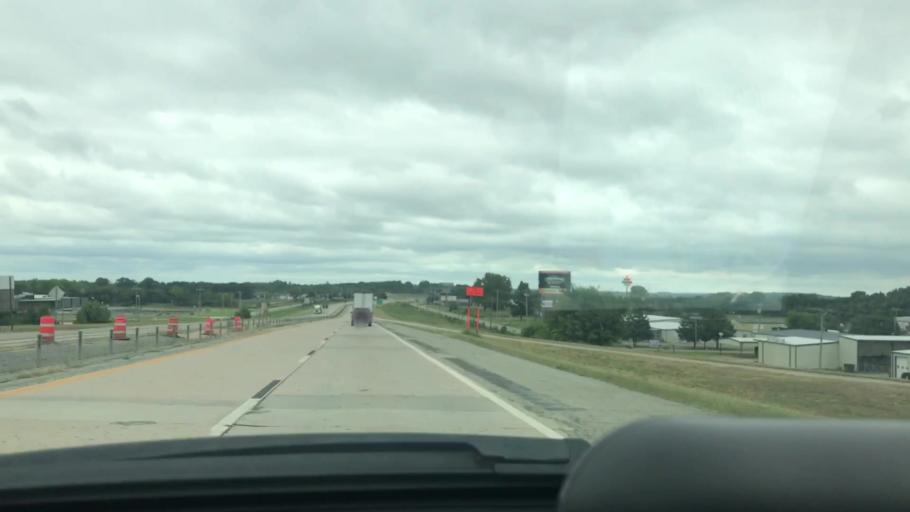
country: US
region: Oklahoma
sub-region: McIntosh County
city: Eufaula
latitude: 35.2961
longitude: -95.5931
